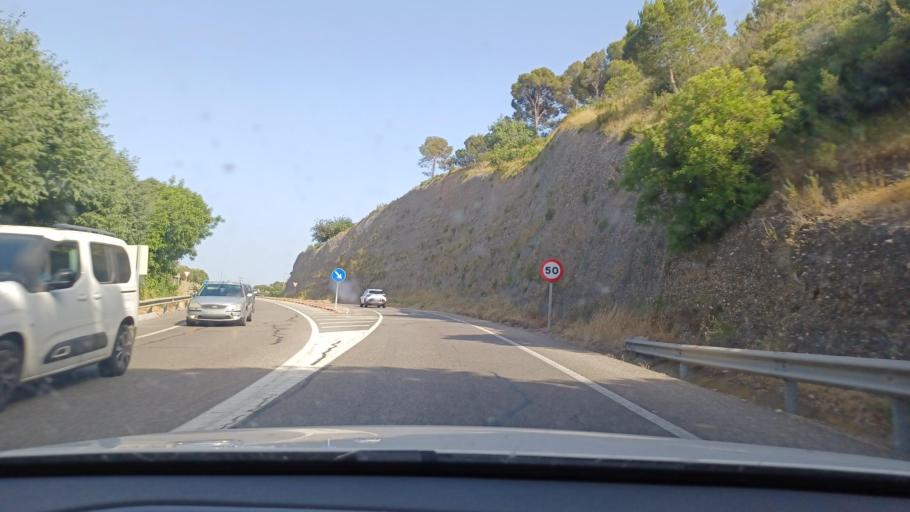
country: ES
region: Catalonia
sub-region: Provincia de Tarragona
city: Tortosa
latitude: 40.7763
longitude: 0.5094
